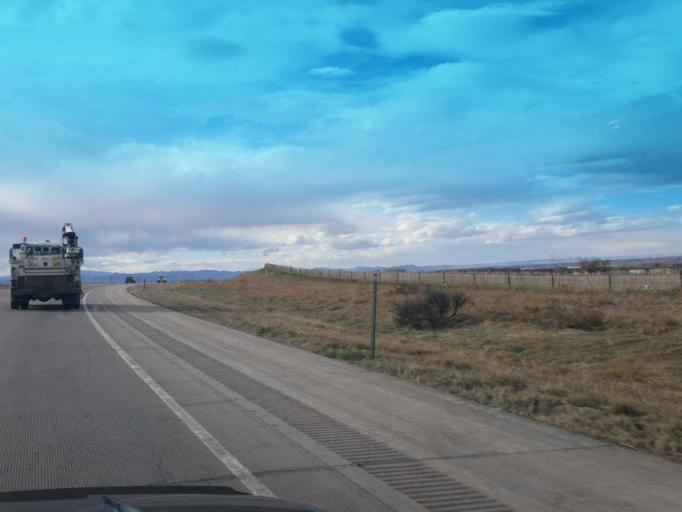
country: US
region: Colorado
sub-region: Weld County
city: Milliken
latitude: 40.3926
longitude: -104.7984
